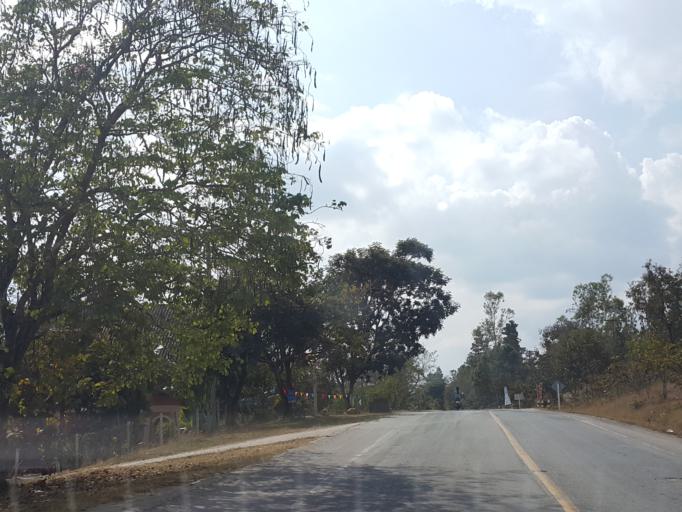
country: TH
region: Chiang Mai
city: Om Koi
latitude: 17.8066
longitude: 98.3661
